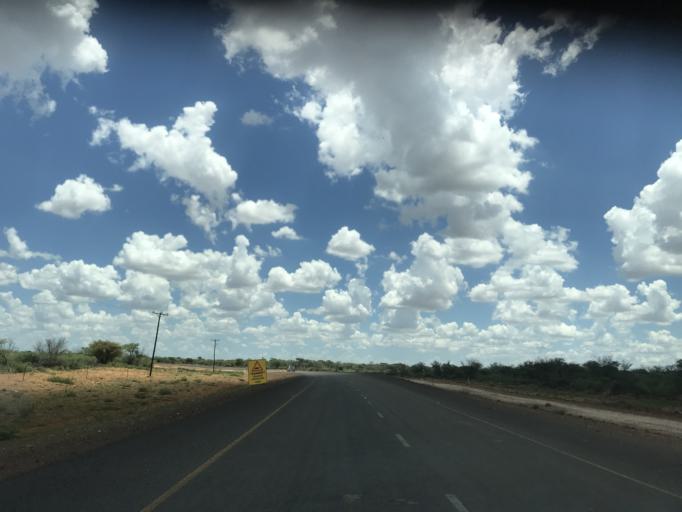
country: BW
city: Mabuli
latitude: -25.8009
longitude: 24.7113
